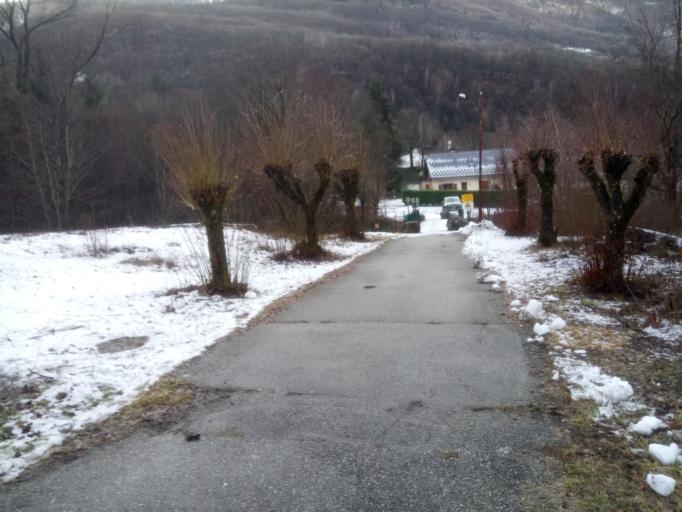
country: FR
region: Rhone-Alpes
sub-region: Departement de la Savoie
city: Saint-Etienne-de-Cuines
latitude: 45.3320
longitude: 6.2890
